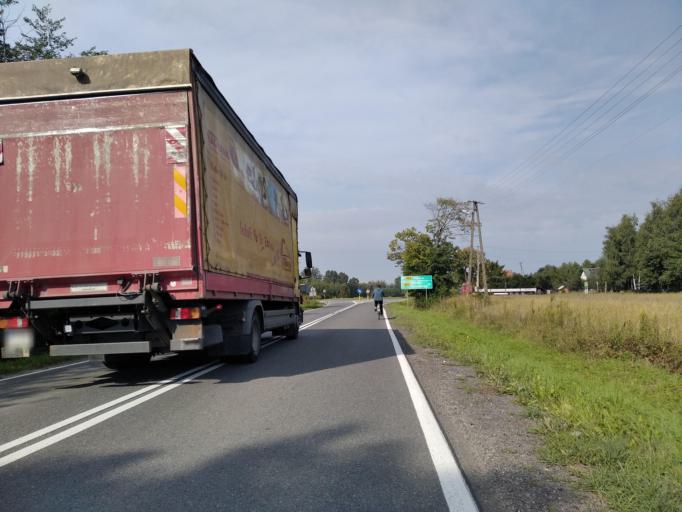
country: PL
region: Subcarpathian Voivodeship
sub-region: Powiat mielecki
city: Przeclaw
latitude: 50.1699
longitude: 21.4924
